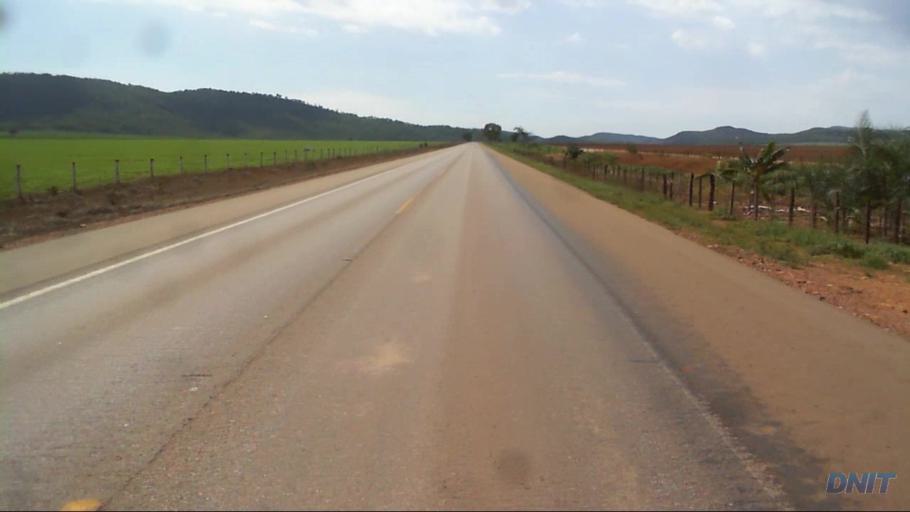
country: BR
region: Goias
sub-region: Barro Alto
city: Barro Alto
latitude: -15.1043
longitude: -48.8481
